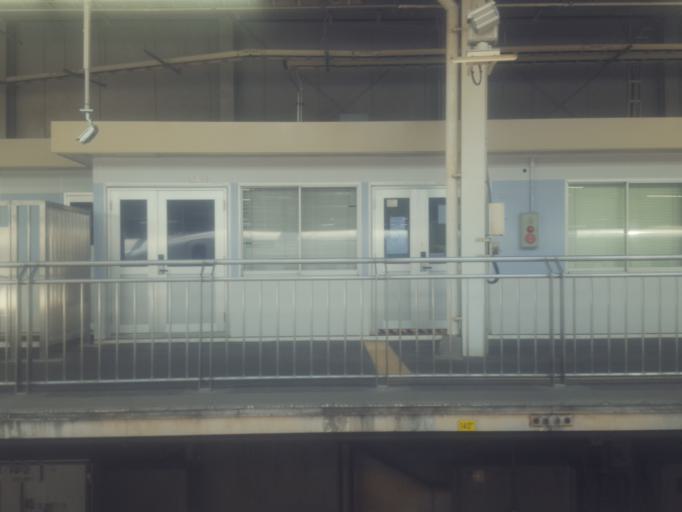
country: JP
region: Osaka
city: Suita
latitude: 34.7338
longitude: 135.5022
